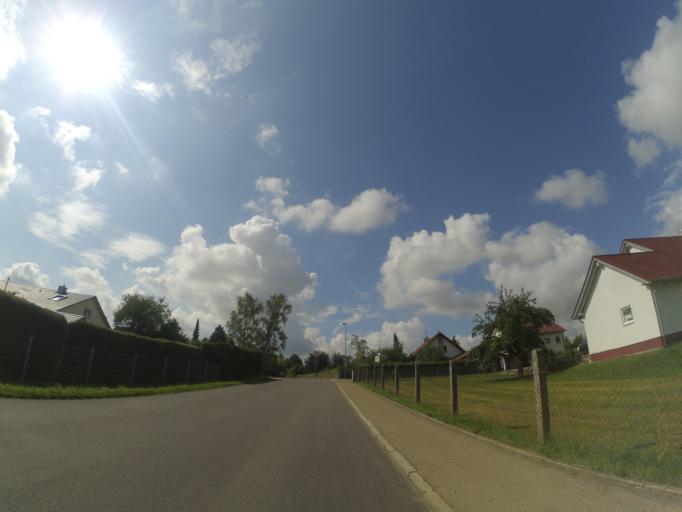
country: DE
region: Baden-Wuerttemberg
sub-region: Tuebingen Region
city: Bernstadt
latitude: 48.4974
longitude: 10.0262
